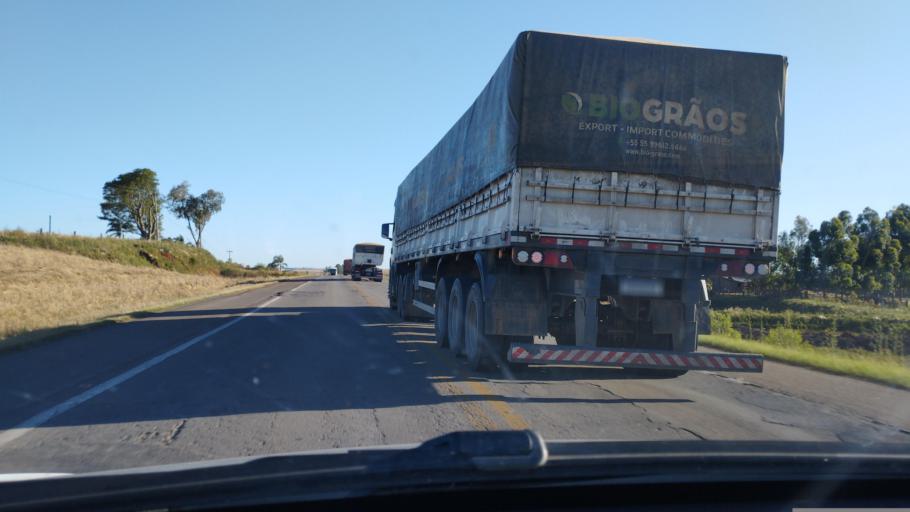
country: BR
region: Rio Grande do Sul
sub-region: Julio De Castilhos
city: Julio de Castilhos
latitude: -29.3815
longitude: -53.6702
